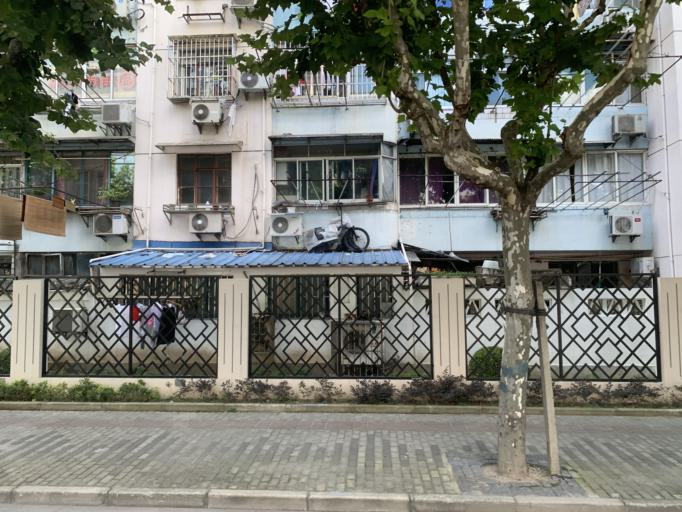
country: CN
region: Shanghai Shi
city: Pudong
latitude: 31.2503
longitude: 121.5566
